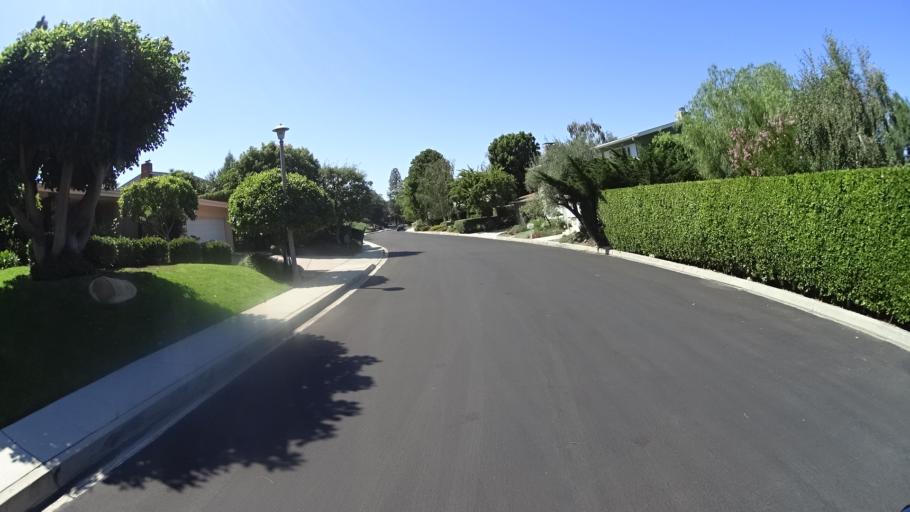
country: US
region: California
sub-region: Los Angeles County
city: Sherman Oaks
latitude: 34.1384
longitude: -118.4914
